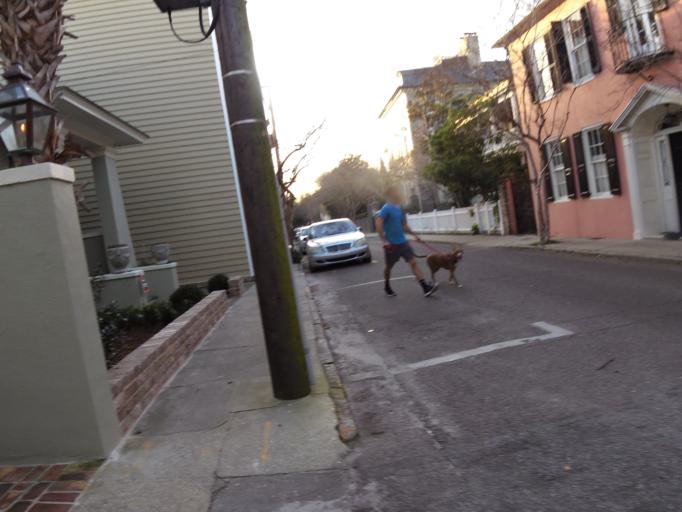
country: US
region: South Carolina
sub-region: Charleston County
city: Charleston
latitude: 32.7744
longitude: -79.9328
